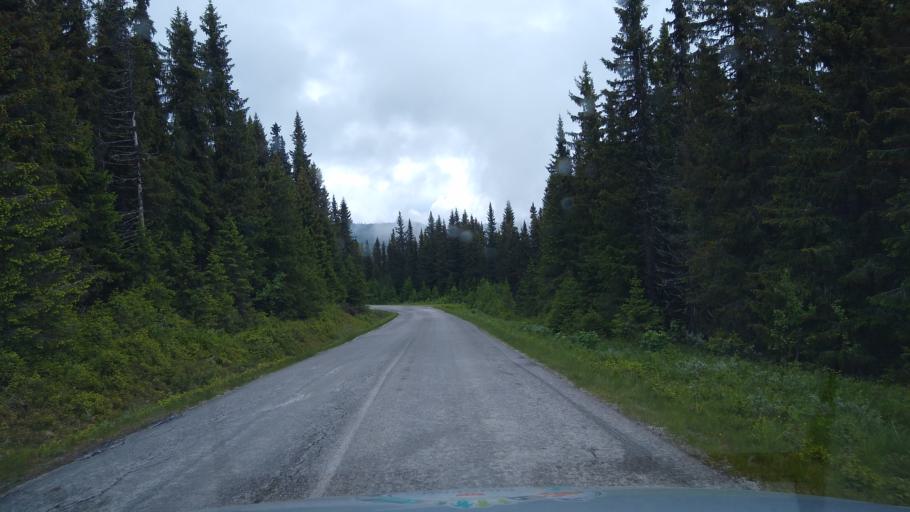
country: NO
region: Oppland
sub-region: Ringebu
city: Ringebu
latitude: 61.4853
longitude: 10.1161
